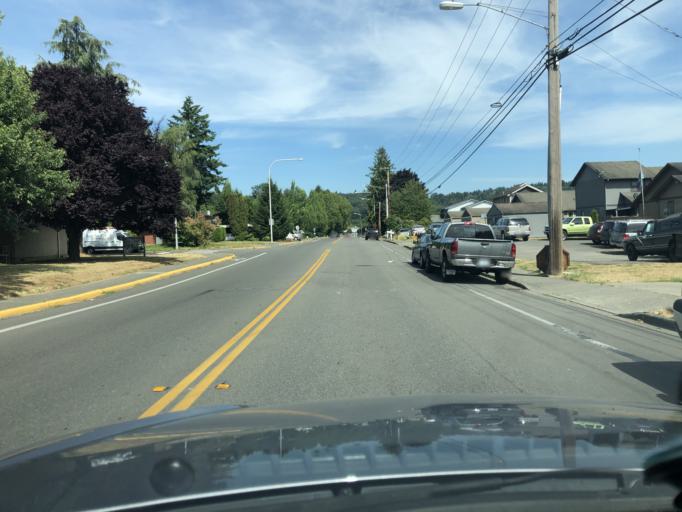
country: US
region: Washington
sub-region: King County
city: Auburn
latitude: 47.3264
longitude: -122.2161
